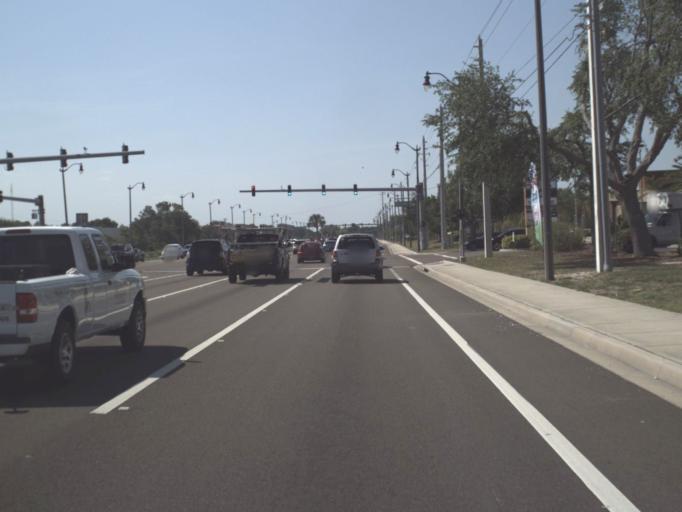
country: US
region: Florida
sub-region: Brevard County
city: Rockledge
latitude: 28.3278
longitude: -80.7199
